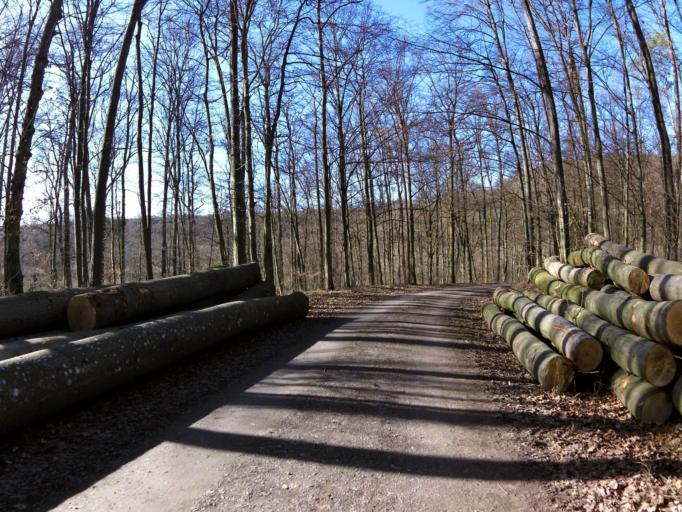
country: DE
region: Bavaria
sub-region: Regierungsbezirk Unterfranken
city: Rimpar
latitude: 49.8555
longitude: 9.9832
